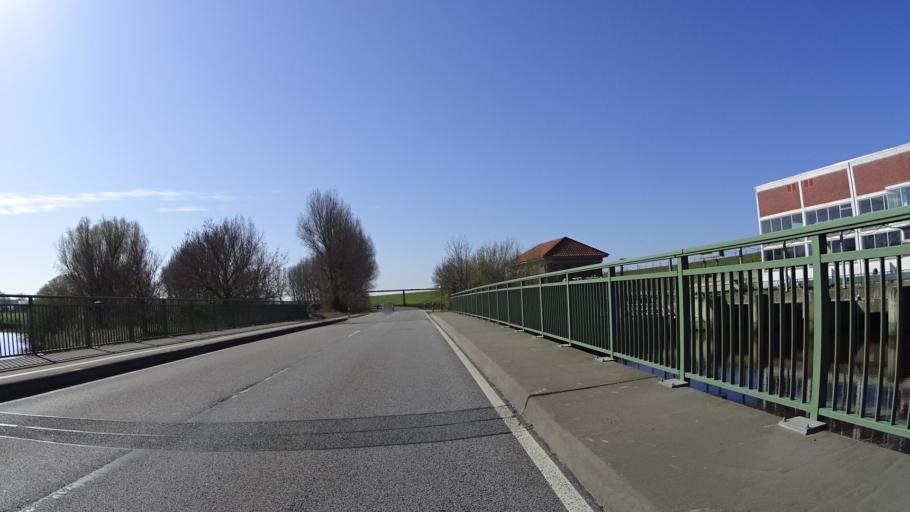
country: DE
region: Lower Saxony
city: Jemgum
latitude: 53.2853
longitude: 7.4047
